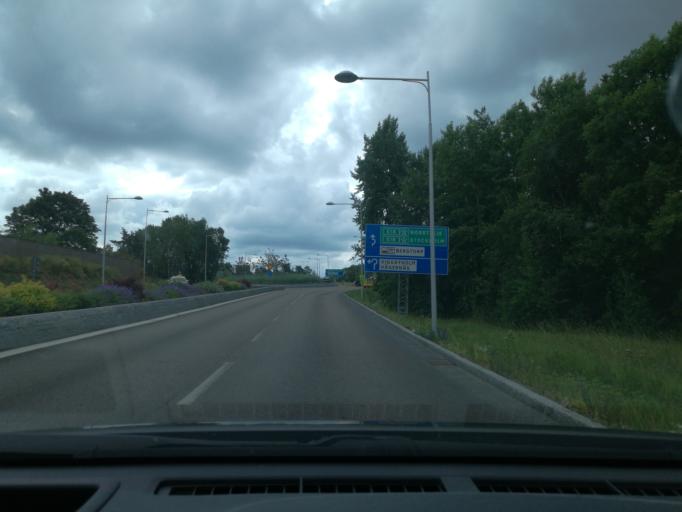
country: SE
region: Stockholm
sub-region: Taby Kommun
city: Taby
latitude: 59.4457
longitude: 18.0954
